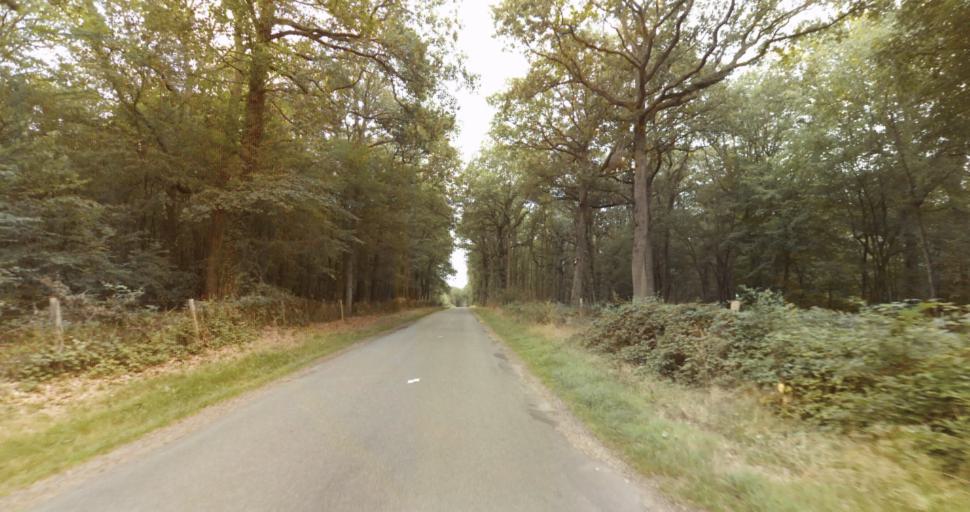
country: FR
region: Haute-Normandie
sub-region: Departement de l'Eure
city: La Couture-Boussey
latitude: 48.8886
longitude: 1.3656
